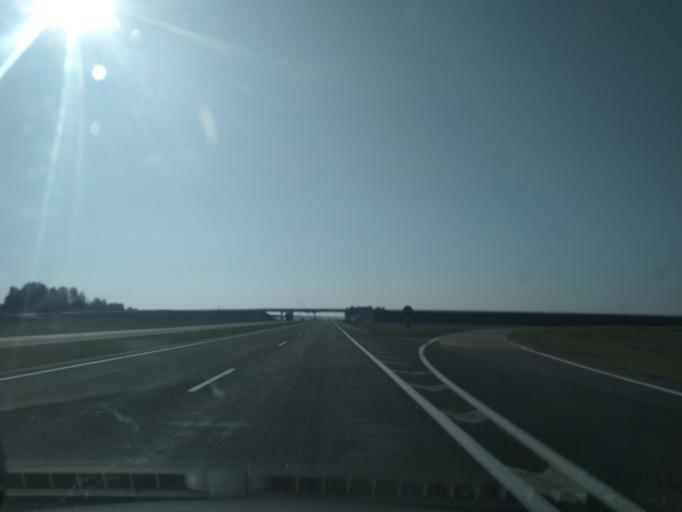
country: BY
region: Brest
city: Antopal'
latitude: 52.3094
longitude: 24.6002
